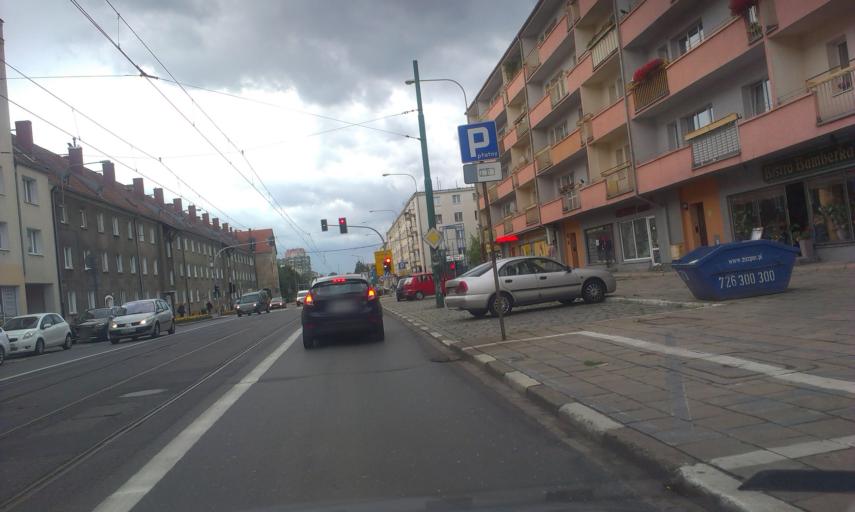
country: PL
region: Greater Poland Voivodeship
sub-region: Poznan
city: Poznan
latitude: 52.4146
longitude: 16.8953
